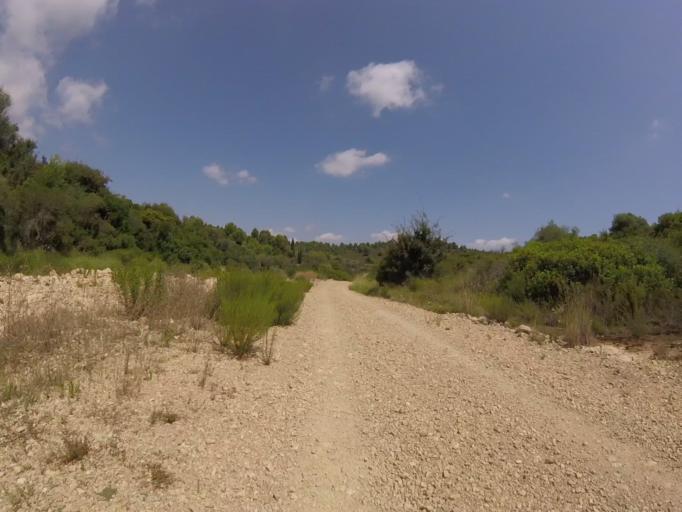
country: ES
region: Valencia
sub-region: Provincia de Castello
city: Torreblanca
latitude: 40.2112
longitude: 0.1394
